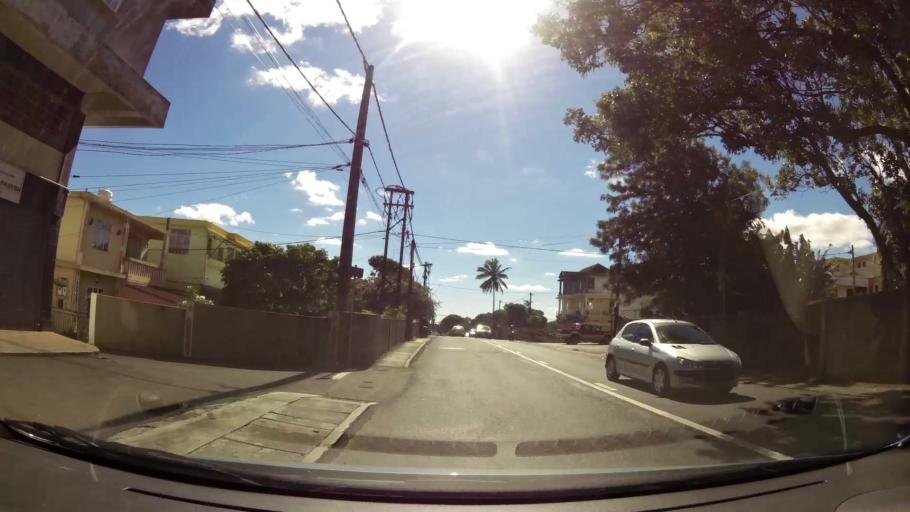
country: MU
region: Plaines Wilhems
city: Vacoas
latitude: -20.2880
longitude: 57.4812
